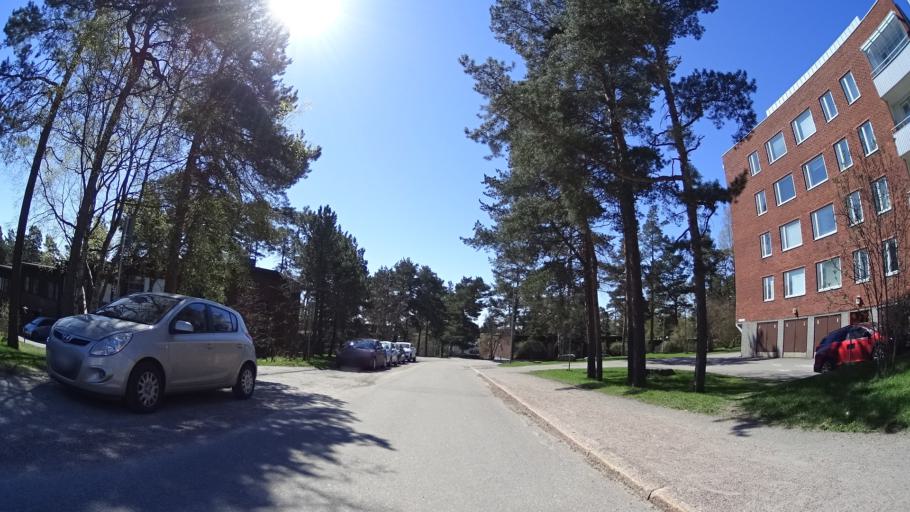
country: FI
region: Uusimaa
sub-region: Helsinki
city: Koukkuniemi
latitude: 60.1577
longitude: 24.7790
